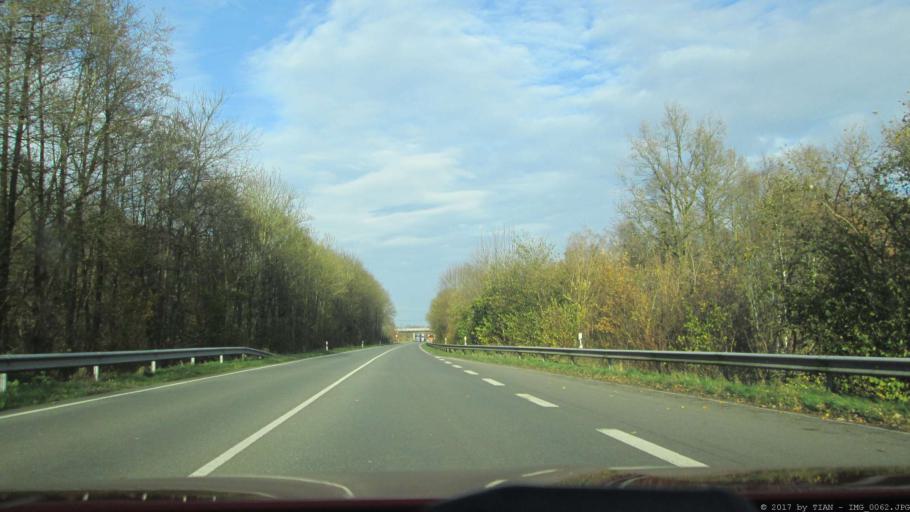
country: DE
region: Lower Saxony
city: Handorf
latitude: 53.3549
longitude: 10.3413
